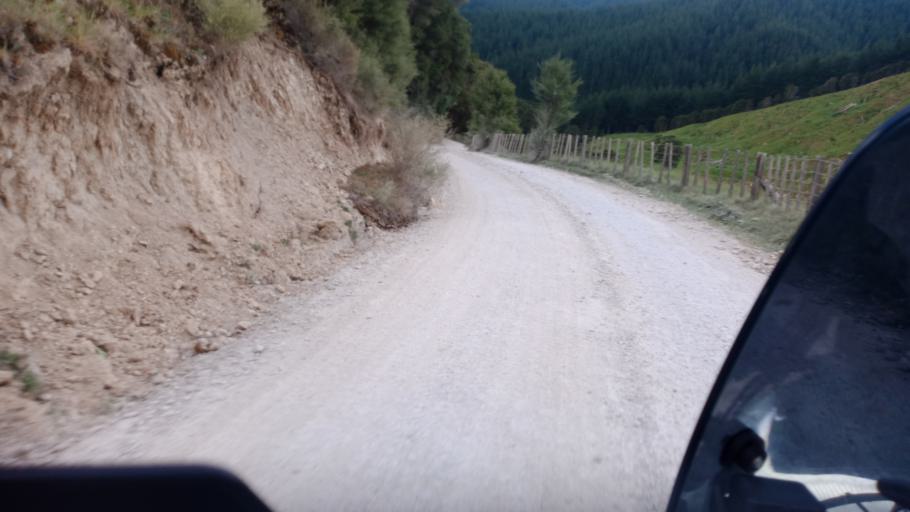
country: NZ
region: Gisborne
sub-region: Gisborne District
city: Gisborne
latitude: -38.4763
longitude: 177.9743
